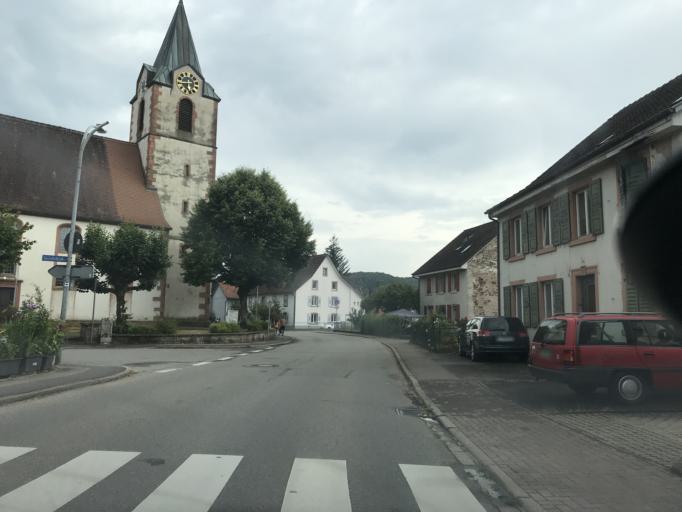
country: DE
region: Baden-Wuerttemberg
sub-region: Freiburg Region
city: Steinen
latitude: 47.6455
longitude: 7.7391
